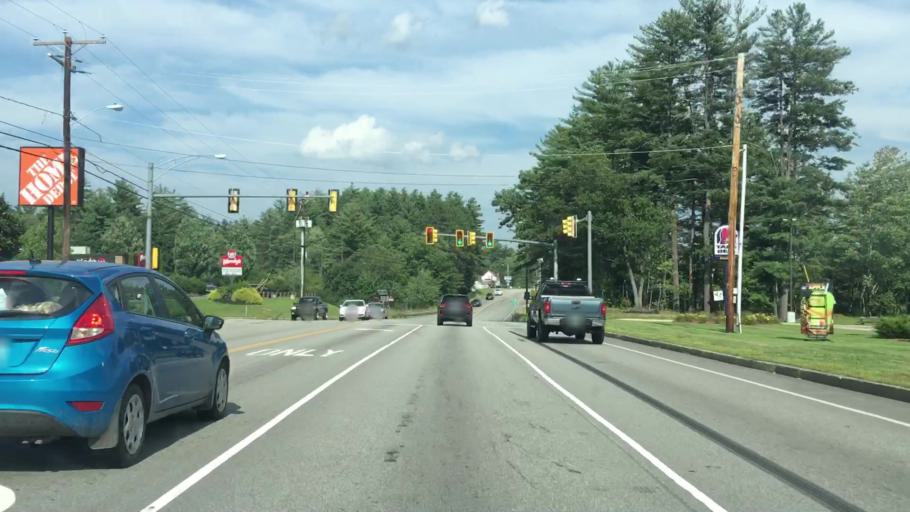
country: US
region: New Hampshire
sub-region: Belknap County
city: Tilton
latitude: 43.4589
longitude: -71.5588
